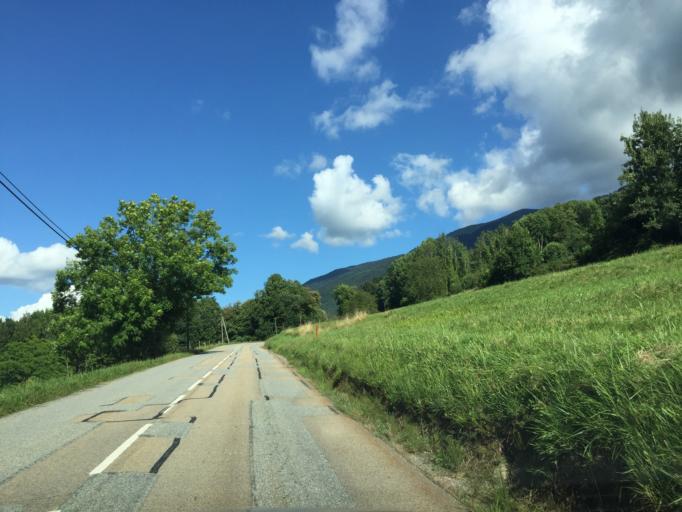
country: FR
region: Rhone-Alpes
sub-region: Departement de la Savoie
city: La Rochette
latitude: 45.4576
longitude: 6.1474
